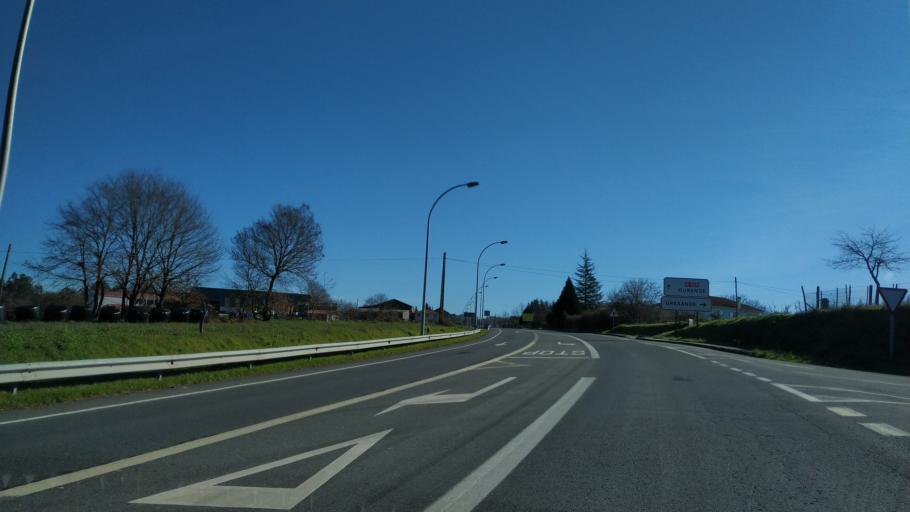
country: ES
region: Galicia
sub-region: Provincia de Pontevedra
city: Silleda
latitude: 42.6834
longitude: -8.1956
